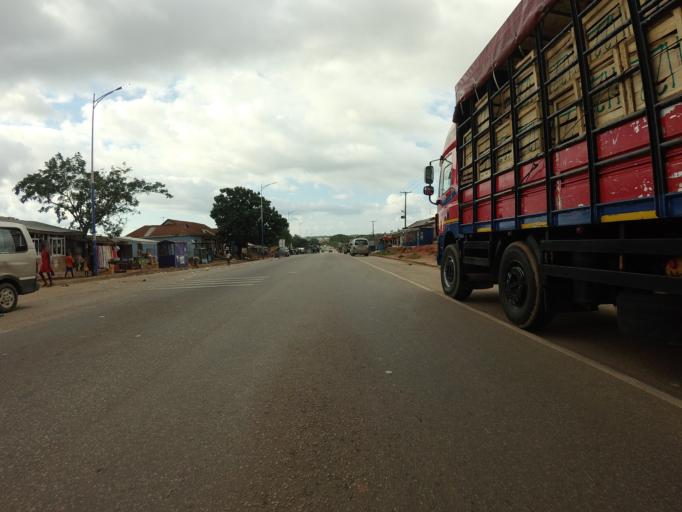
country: GH
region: Ashanti
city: Tafo
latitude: 6.8166
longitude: -1.6482
